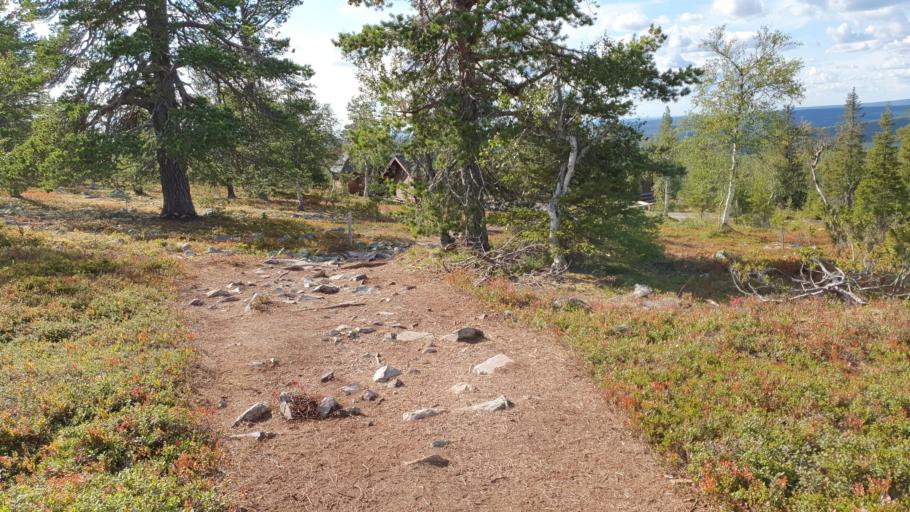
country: FI
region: Lapland
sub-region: Tunturi-Lappi
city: Kolari
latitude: 67.6151
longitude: 24.2558
